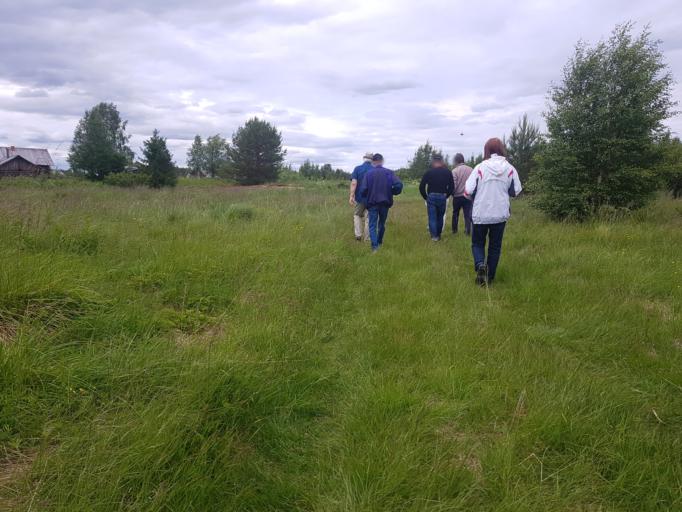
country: RU
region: Republic of Karelia
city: Yushkozero
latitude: 65.1637
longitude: 32.0127
